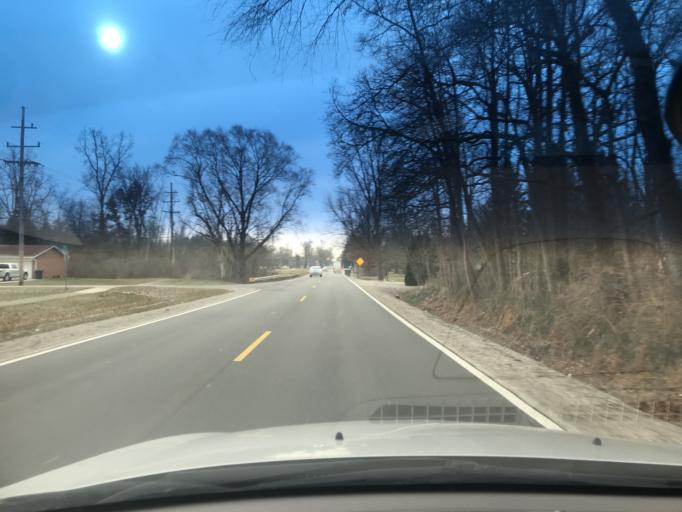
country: US
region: Michigan
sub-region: Macomb County
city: Shelby
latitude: 42.6865
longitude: -83.0542
